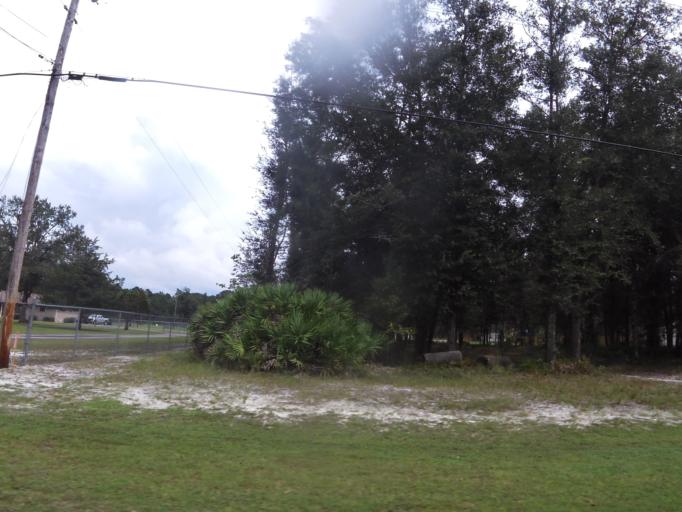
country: US
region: Florida
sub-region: Clay County
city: Middleburg
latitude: 30.1194
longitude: -81.9618
